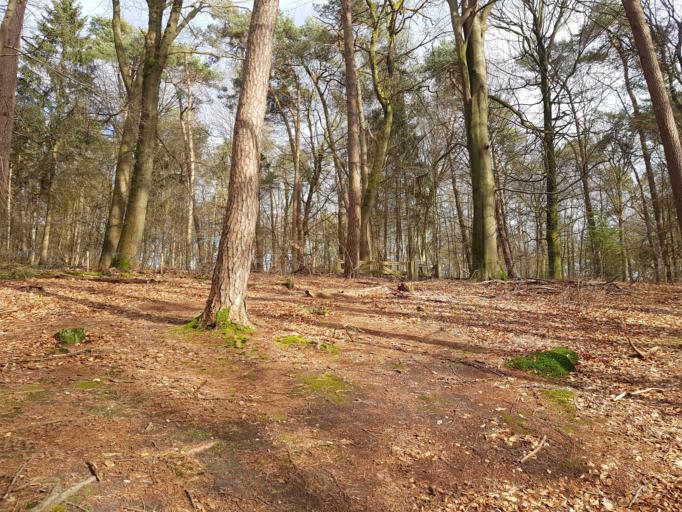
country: NL
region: Gelderland
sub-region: Gemeente Rheden
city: Velp
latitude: 52.0118
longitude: 5.9874
